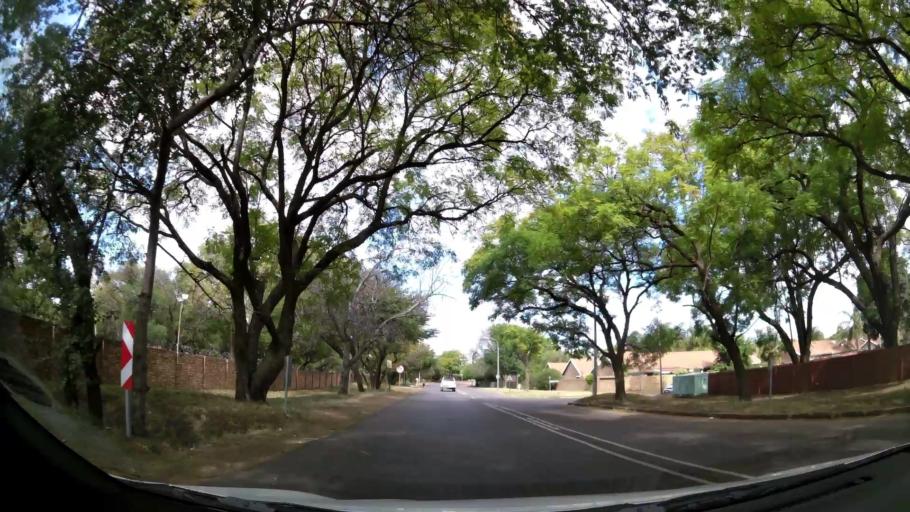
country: ZA
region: Limpopo
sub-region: Waterberg District Municipality
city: Warmbaths
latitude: -24.8864
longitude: 28.2845
